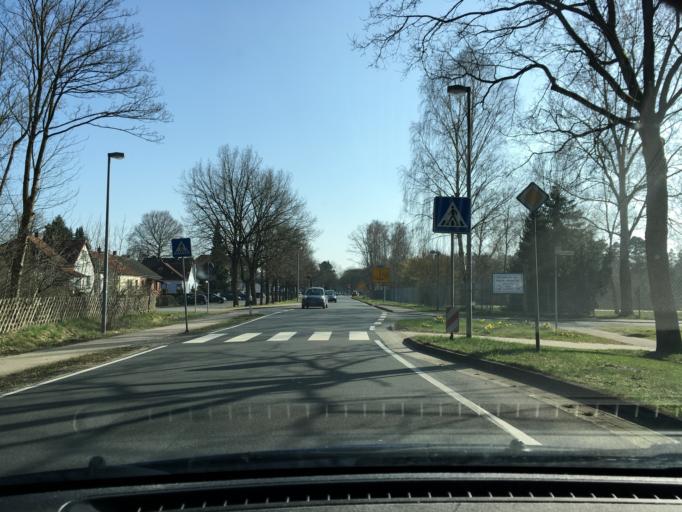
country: DE
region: Lower Saxony
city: Winsen
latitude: 52.6358
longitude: 9.9304
